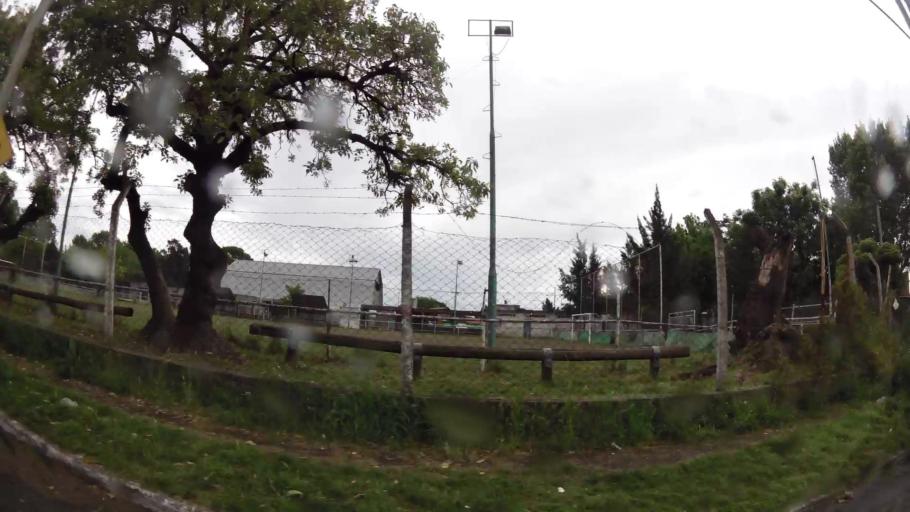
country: AR
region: Buenos Aires
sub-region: Partido de Quilmes
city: Quilmes
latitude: -34.7659
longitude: -58.2303
